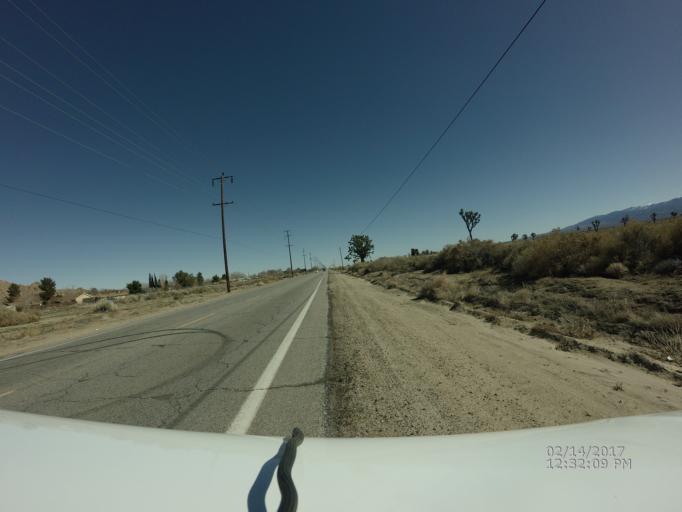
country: US
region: California
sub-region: Los Angeles County
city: Lake Los Angeles
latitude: 34.5799
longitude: -117.8610
